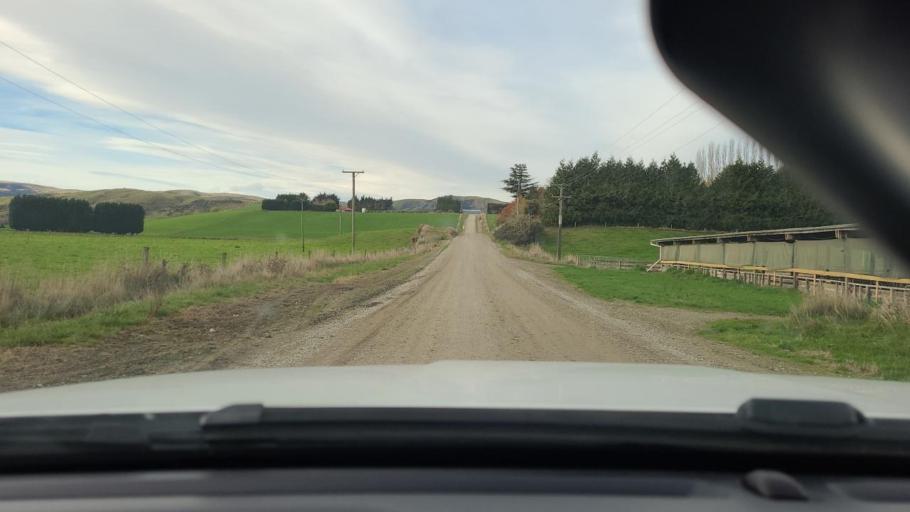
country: NZ
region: Southland
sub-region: Gore District
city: Gore
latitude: -45.8343
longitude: 168.8368
